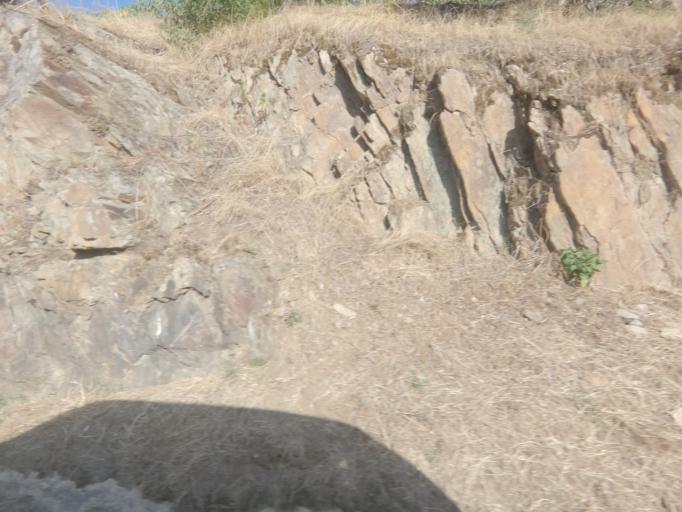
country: PT
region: Vila Real
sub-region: Sabrosa
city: Vilela
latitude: 41.2020
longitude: -7.5398
